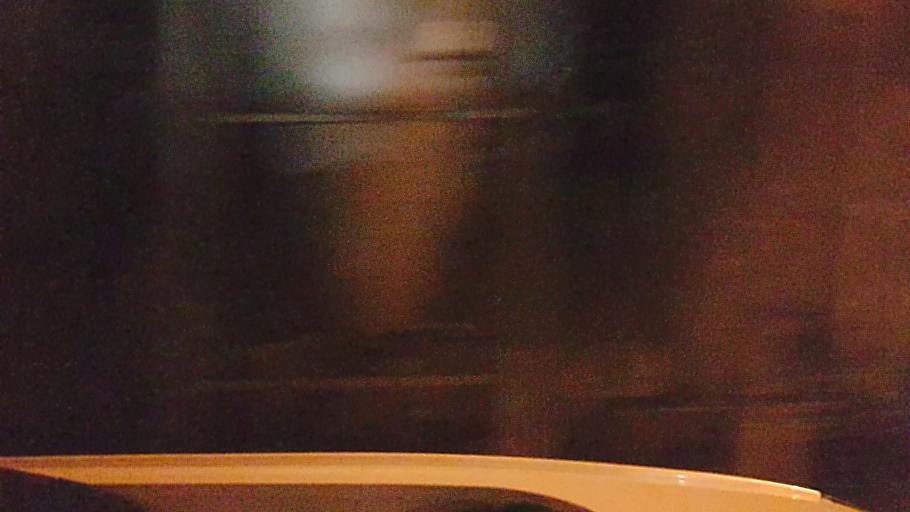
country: IL
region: Central District
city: Hod HaSharon
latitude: 32.1634
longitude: 34.8763
